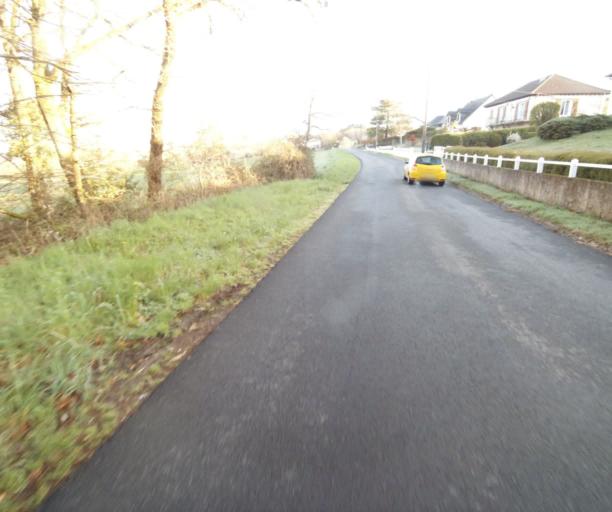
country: FR
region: Limousin
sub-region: Departement de la Correze
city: Correze
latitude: 45.3146
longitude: 1.8429
